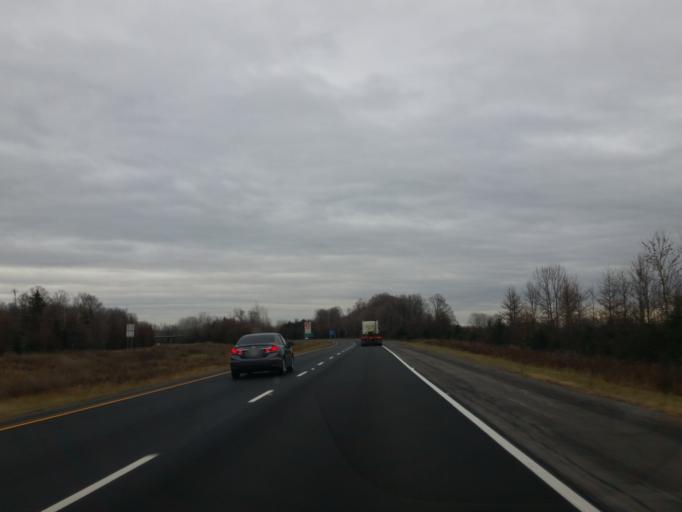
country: CA
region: Quebec
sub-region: Capitale-Nationale
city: Saint-Marc-des-Carrieres
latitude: 46.6013
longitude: -72.0820
